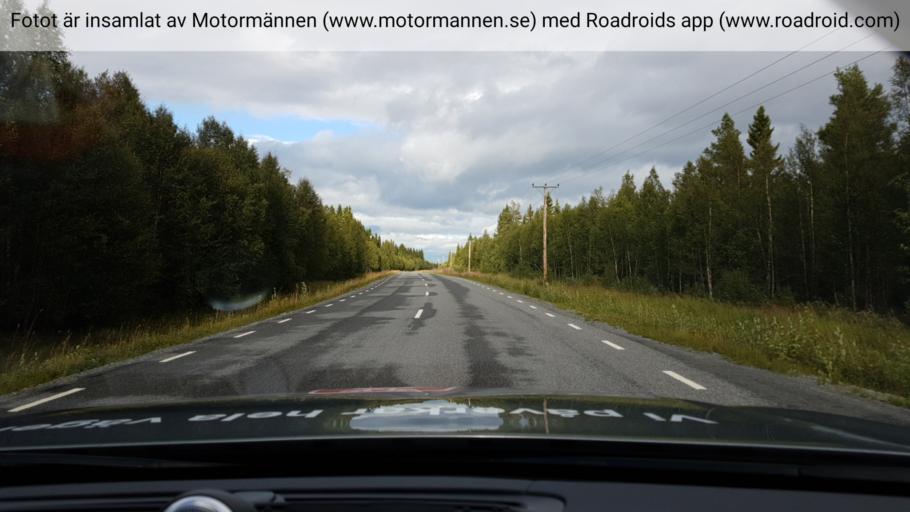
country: SE
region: Jaemtland
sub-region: Krokoms Kommun
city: Krokom
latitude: 63.6461
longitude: 14.4448
